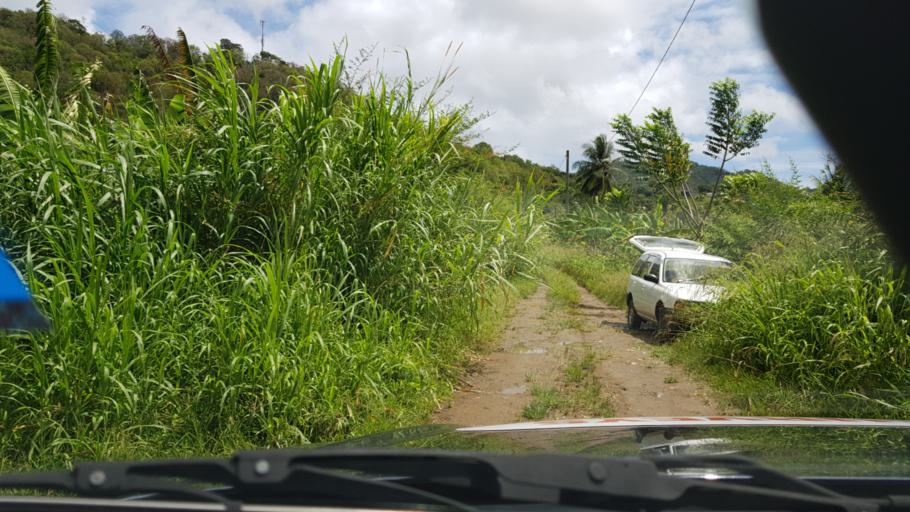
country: LC
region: Anse-la-Raye
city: Anse La Raye
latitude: 13.9560
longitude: -61.0243
